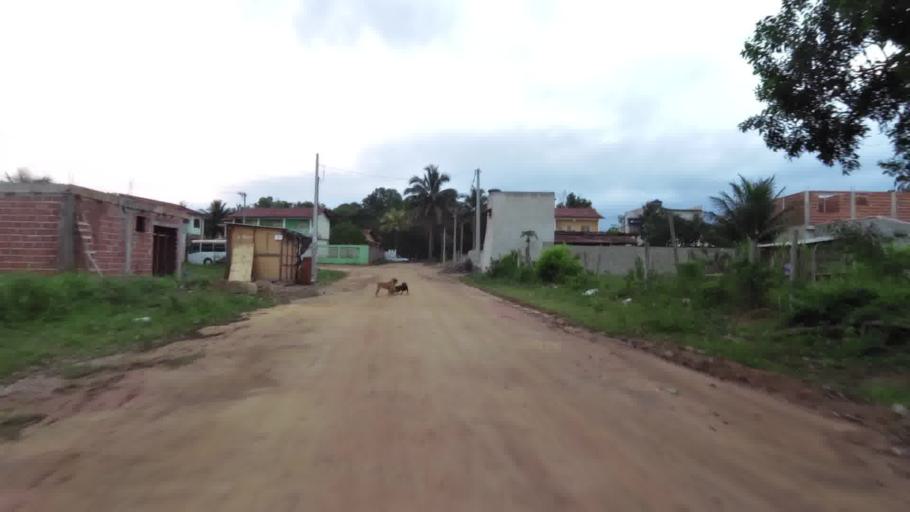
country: BR
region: Espirito Santo
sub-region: Piuma
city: Piuma
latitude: -20.8087
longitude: -40.6329
